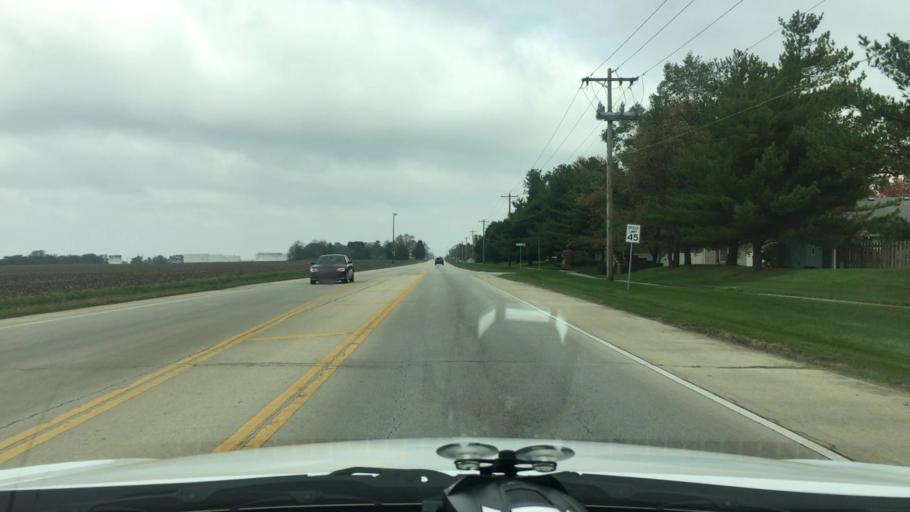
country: US
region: Illinois
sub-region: Champaign County
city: Champaign
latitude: 40.0998
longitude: -88.3144
